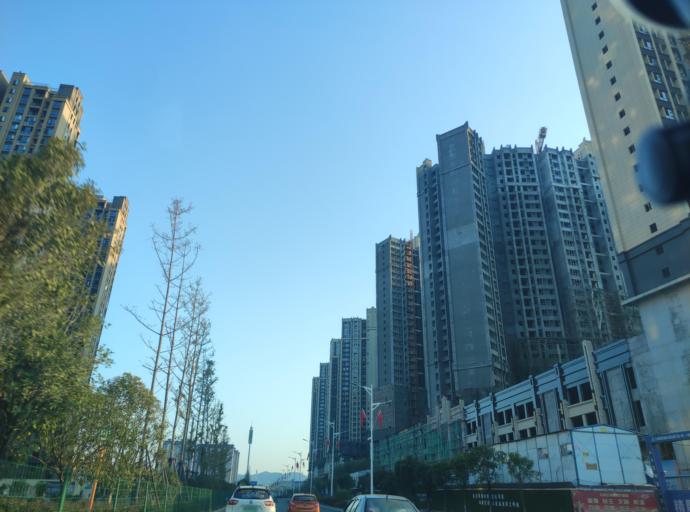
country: CN
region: Jiangxi Sheng
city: Pingxiang
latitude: 27.6353
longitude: 113.8296
